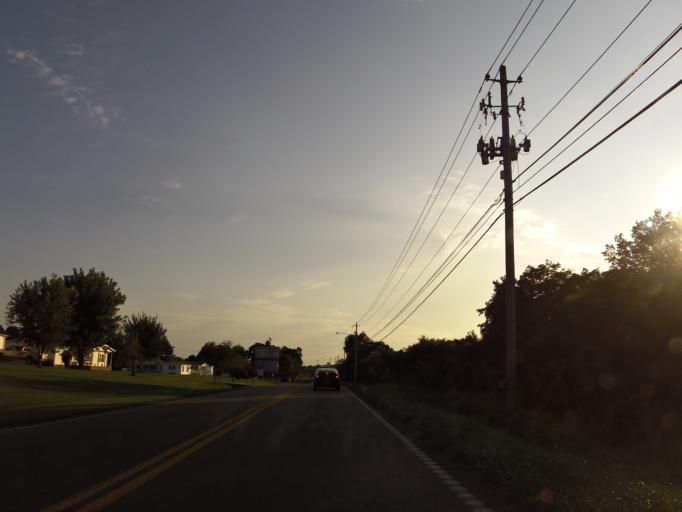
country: US
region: Tennessee
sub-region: McMinn County
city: Athens
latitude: 35.5088
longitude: -84.5591
